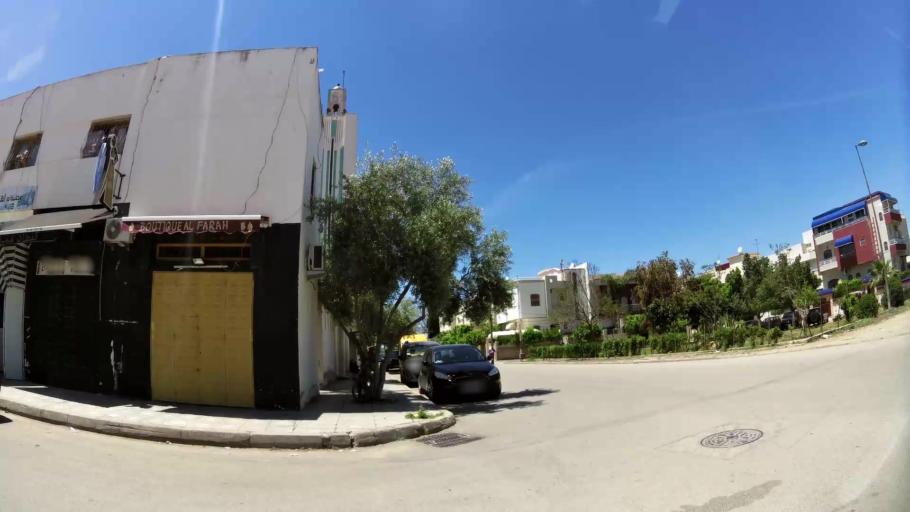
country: MA
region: Fes-Boulemane
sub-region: Fes
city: Fes
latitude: 34.0256
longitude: -5.0120
